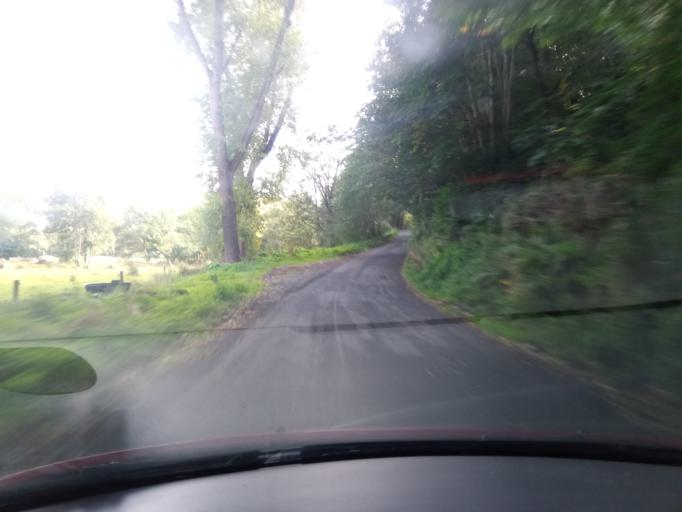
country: GB
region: Scotland
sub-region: The Scottish Borders
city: Kelso
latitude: 55.5037
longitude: -2.3492
